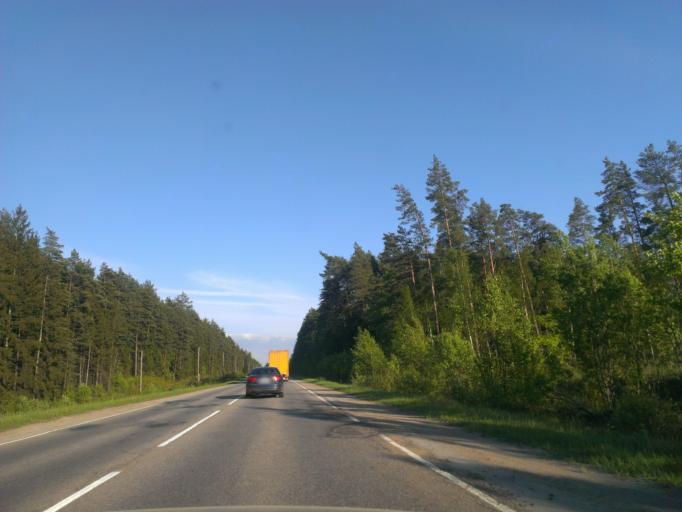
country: LV
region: Baldone
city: Baldone
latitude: 56.7585
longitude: 24.3249
